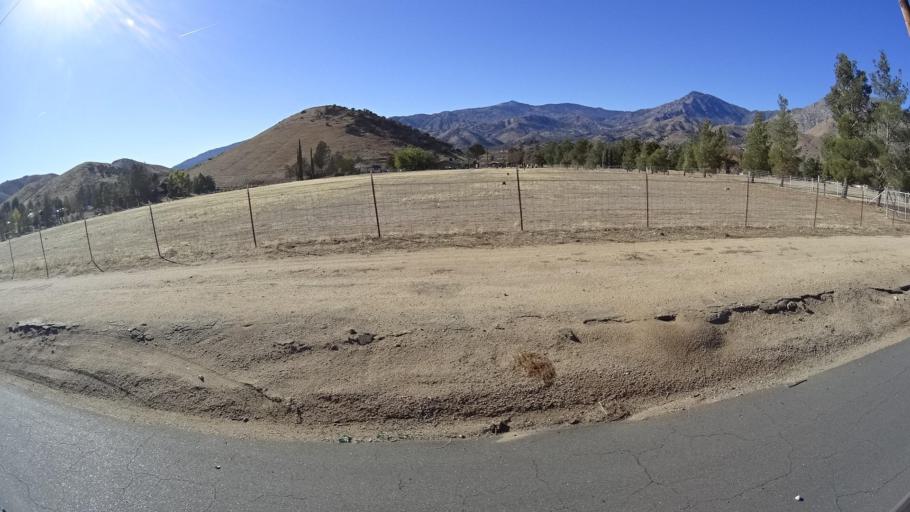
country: US
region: California
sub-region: Kern County
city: Wofford Heights
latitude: 35.7042
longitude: -118.4233
